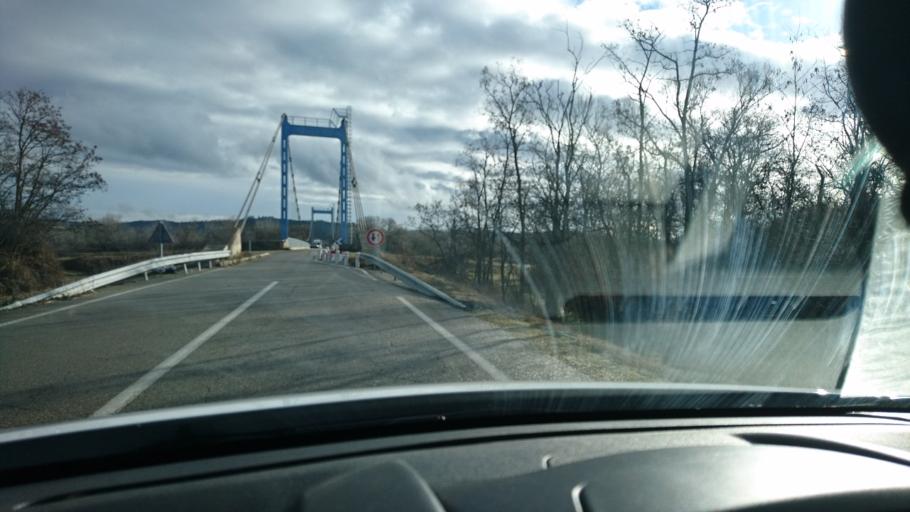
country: FR
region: Provence-Alpes-Cote d'Azur
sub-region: Departement du Vaucluse
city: Mondragon
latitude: 44.2458
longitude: 4.7000
